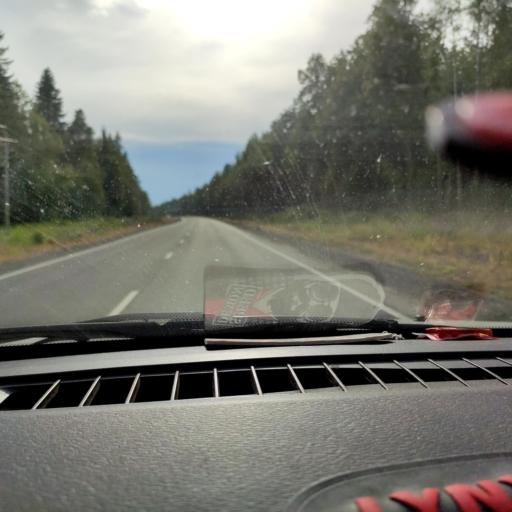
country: RU
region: Perm
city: Polazna
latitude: 58.1954
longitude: 56.2632
